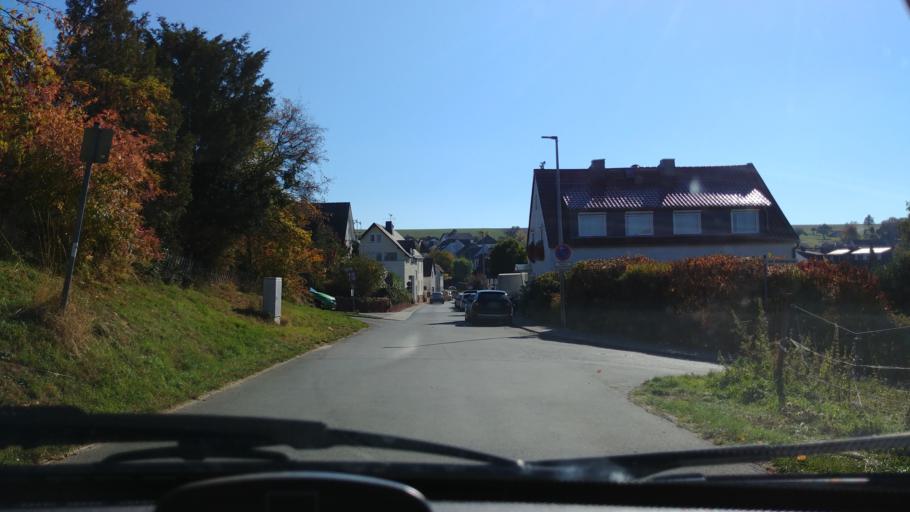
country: DE
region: Hesse
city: Burg Hohenstein
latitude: 50.2119
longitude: 8.0896
